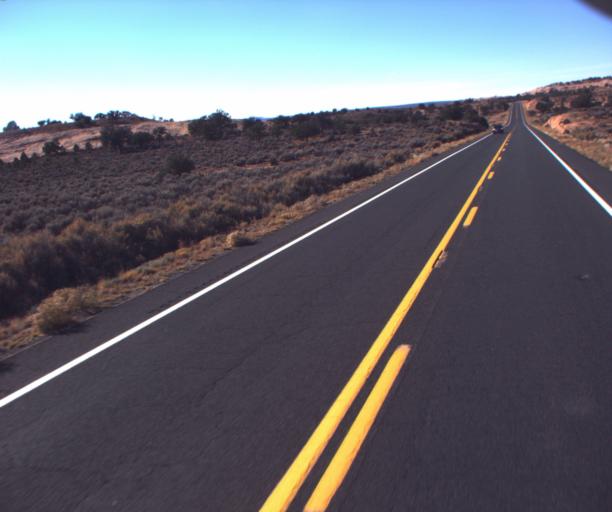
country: US
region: Arizona
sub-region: Coconino County
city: Kaibito
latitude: 36.5570
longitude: -110.7138
